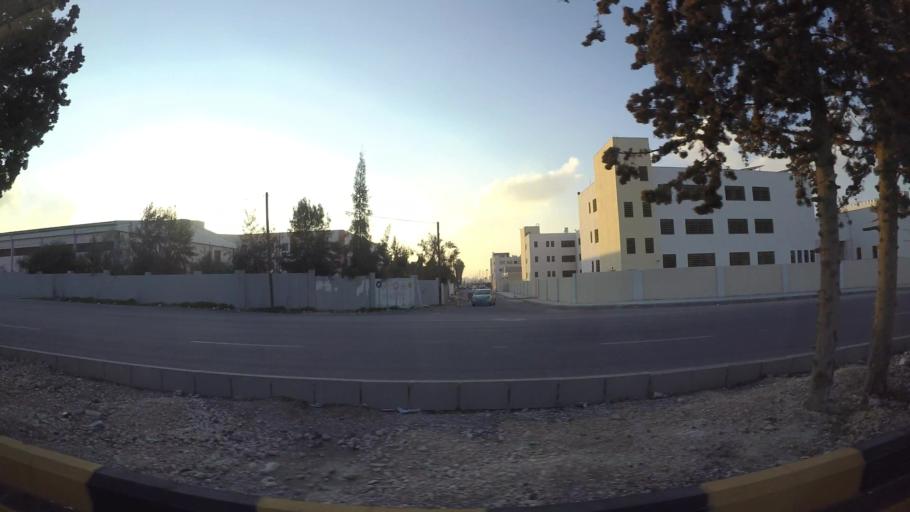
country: JO
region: Amman
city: Al Quwaysimah
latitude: 31.9096
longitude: 35.9230
